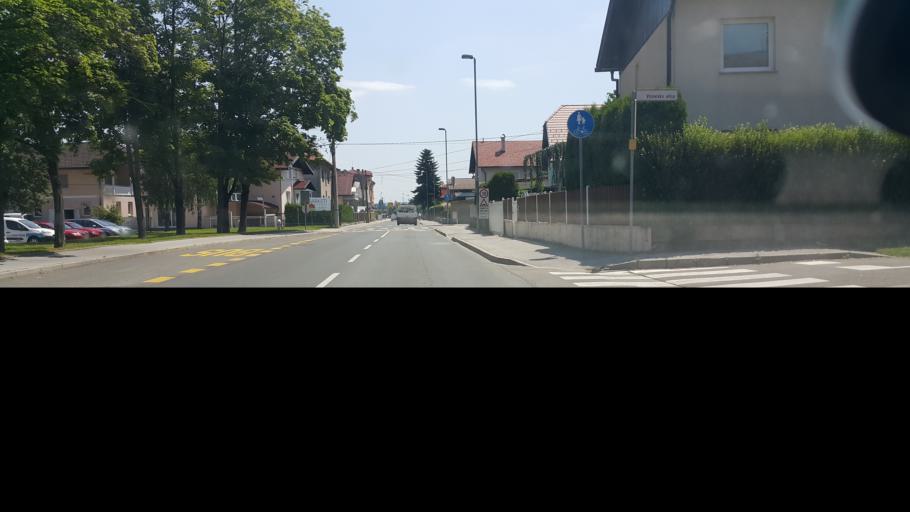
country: SI
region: Maribor
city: Kamnica
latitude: 46.5541
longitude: 15.6189
